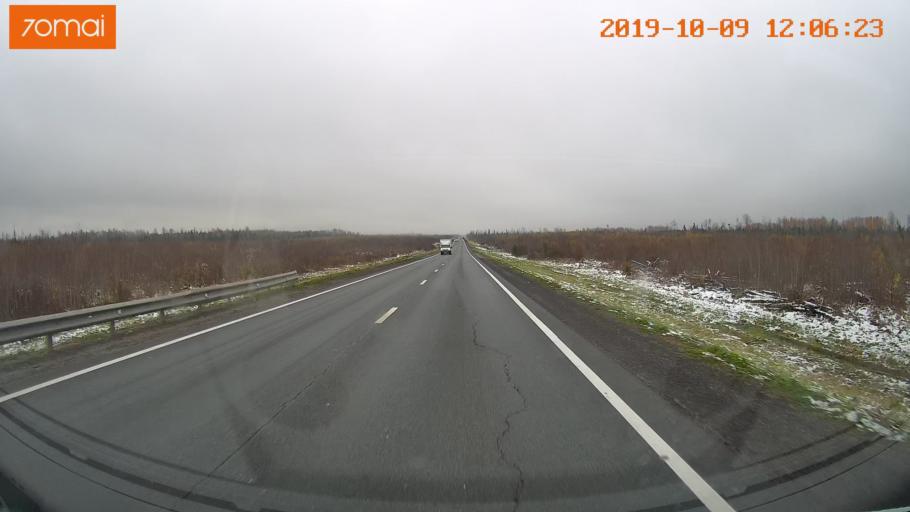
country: RU
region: Jaroslavl
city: Prechistoye
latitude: 58.6153
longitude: 40.3348
